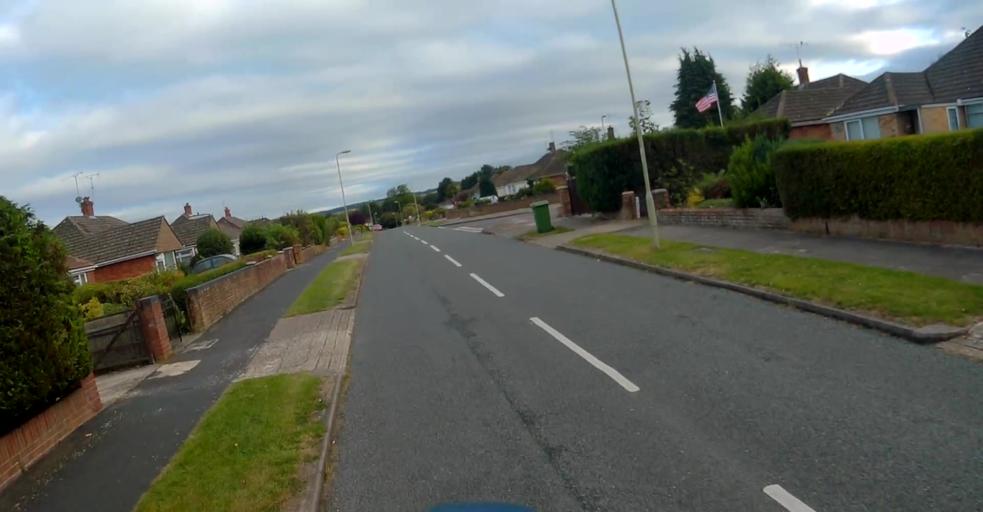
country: GB
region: England
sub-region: Hampshire
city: Basingstoke
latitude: 51.2531
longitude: -1.1205
